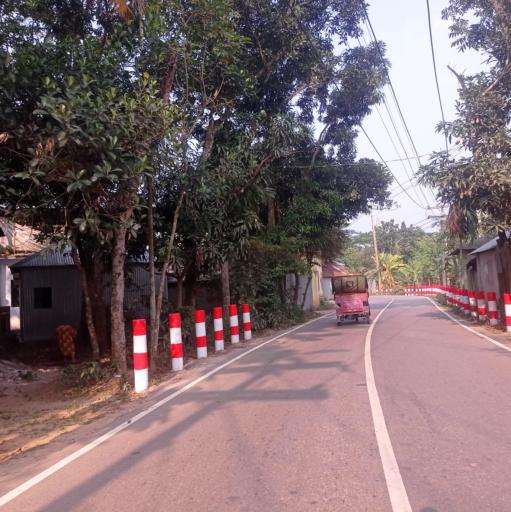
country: BD
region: Dhaka
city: Bhairab Bazar
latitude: 24.0788
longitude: 90.8482
